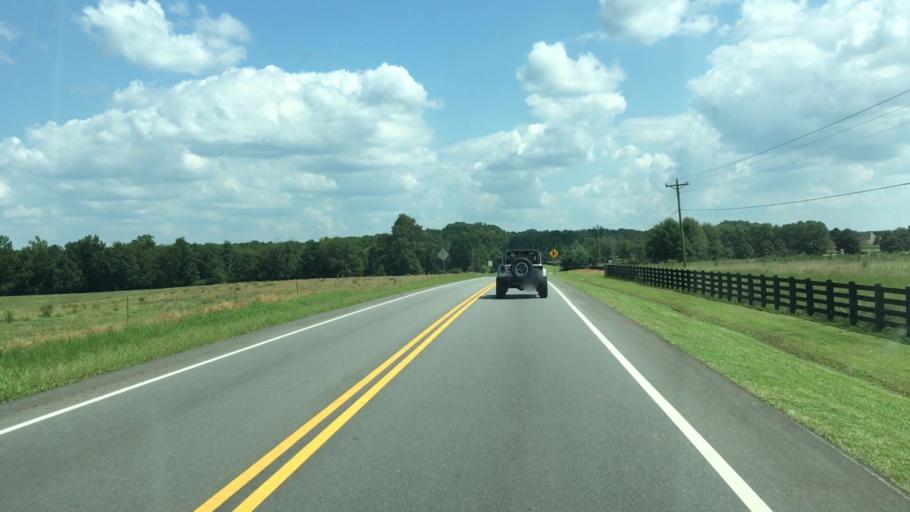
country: US
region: Georgia
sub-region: Morgan County
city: Madison
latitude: 33.5375
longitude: -83.4595
